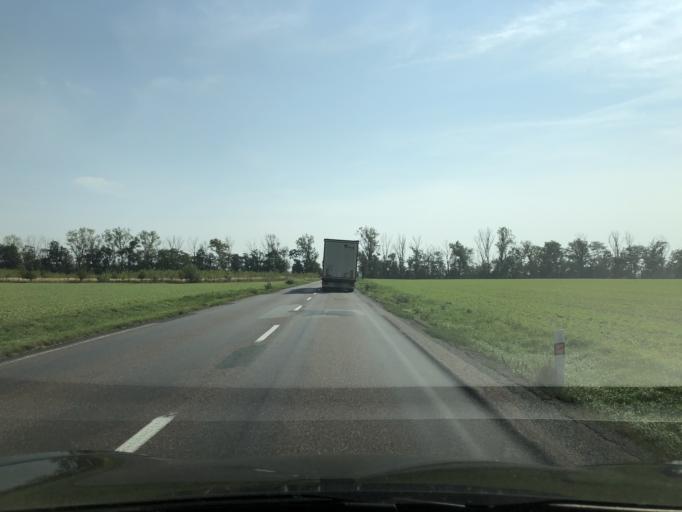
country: CZ
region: South Moravian
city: Brezi
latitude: 48.8239
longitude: 16.5445
